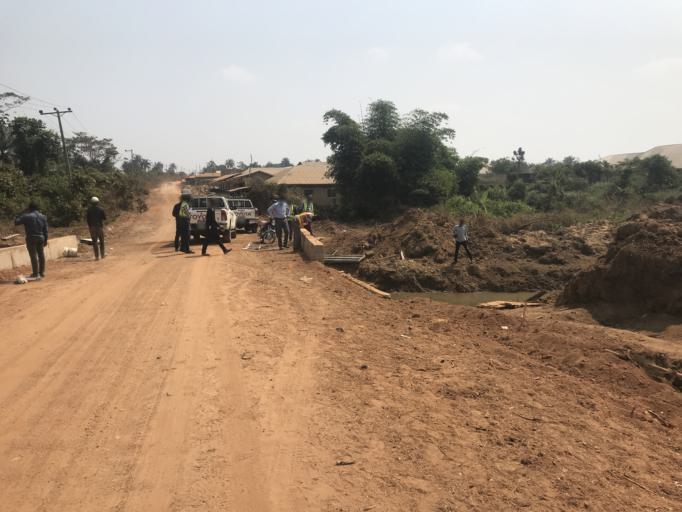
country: NG
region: Osun
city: Osogbo
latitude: 7.7661
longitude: 4.6108
